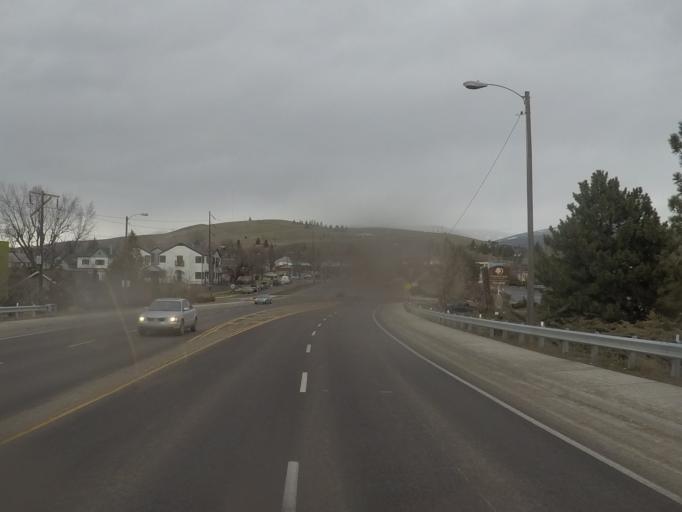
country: US
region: Montana
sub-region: Missoula County
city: Missoula
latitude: 46.8677
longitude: -113.9877
